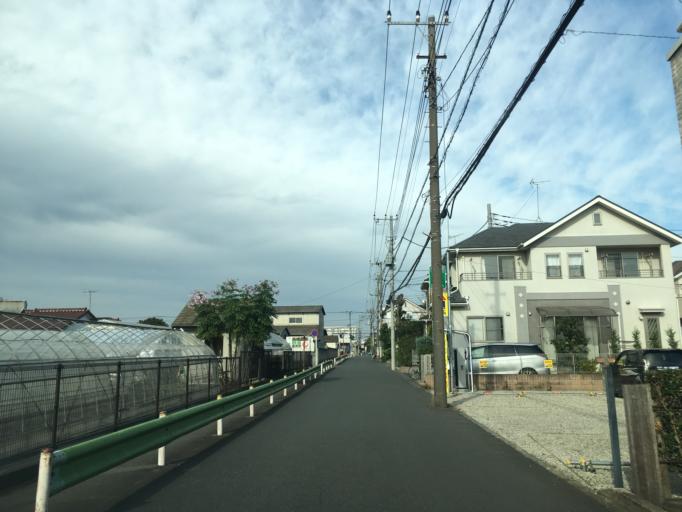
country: JP
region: Tokyo
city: Tanashicho
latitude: 35.7345
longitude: 139.5065
